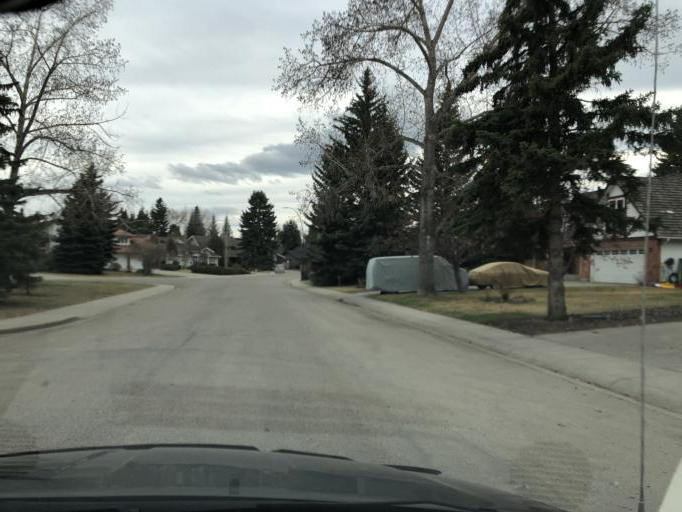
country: CA
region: Alberta
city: Calgary
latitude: 50.9436
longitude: -114.0556
